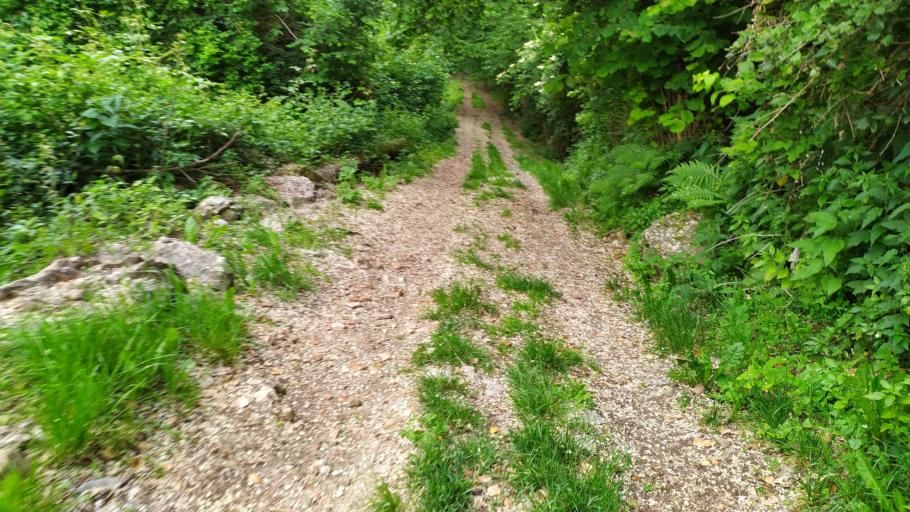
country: IT
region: Veneto
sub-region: Provincia di Vicenza
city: Torrebelvicino
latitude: 45.6903
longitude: 11.3113
